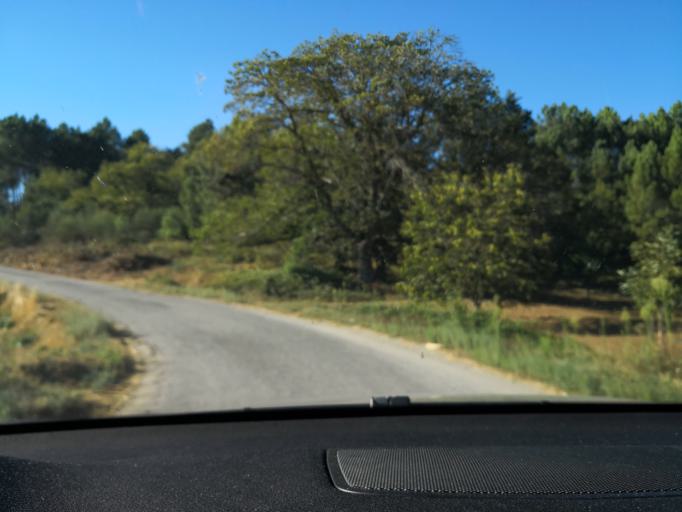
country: PT
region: Vila Real
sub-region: Sabrosa
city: Vilela
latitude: 41.2425
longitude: -7.6185
